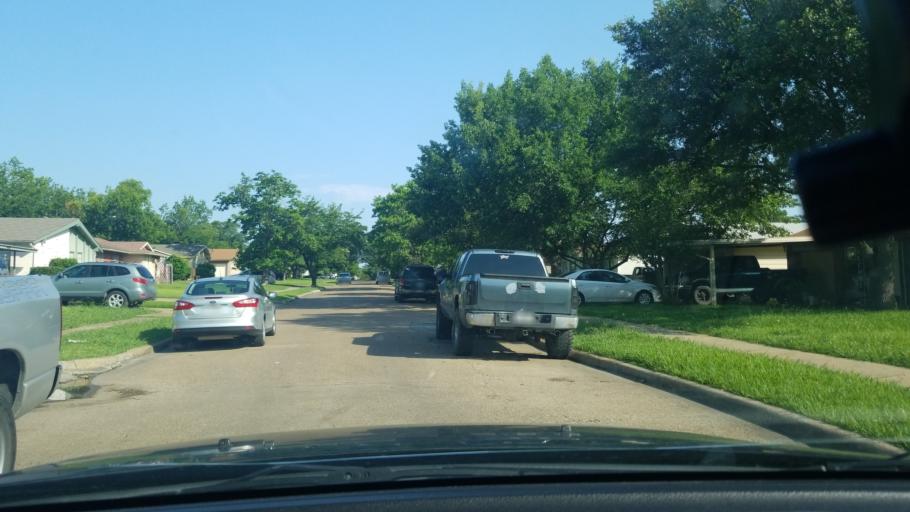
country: US
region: Texas
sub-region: Dallas County
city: Mesquite
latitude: 32.8245
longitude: -96.6328
